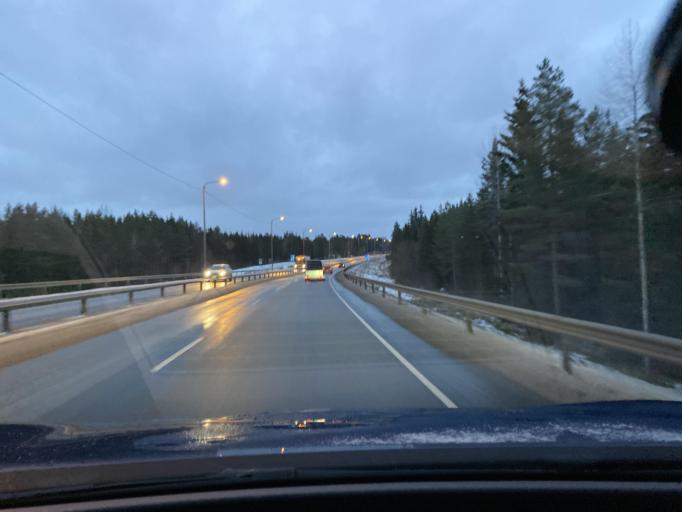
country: FI
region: Satakunta
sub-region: Rauma
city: Rauma
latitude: 61.1438
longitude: 21.5529
